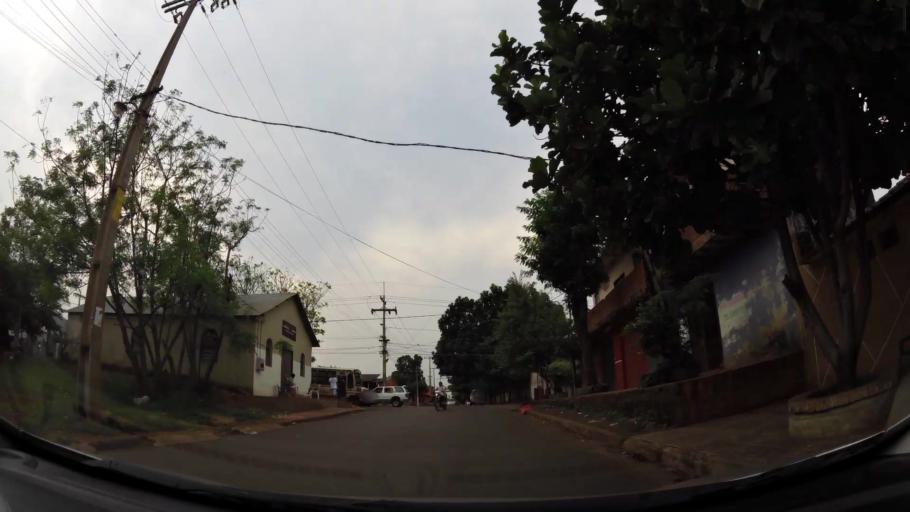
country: PY
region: Alto Parana
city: Presidente Franco
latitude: -25.5371
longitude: -54.6134
